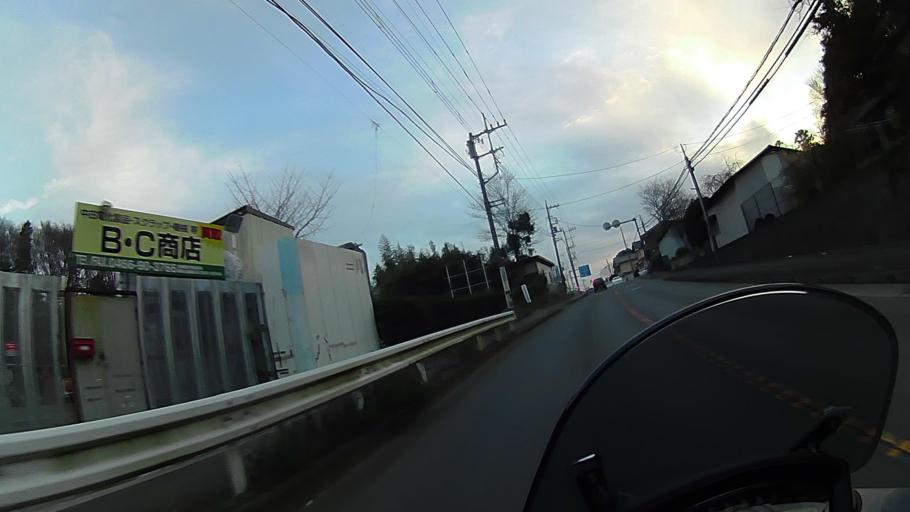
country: JP
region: Kanagawa
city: Atsugi
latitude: 35.4068
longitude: 139.4141
